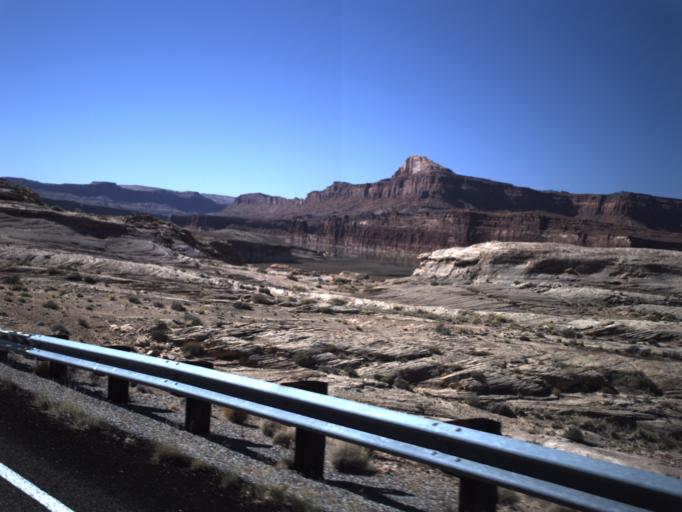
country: US
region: Utah
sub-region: San Juan County
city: Blanding
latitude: 37.8987
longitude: -110.3799
